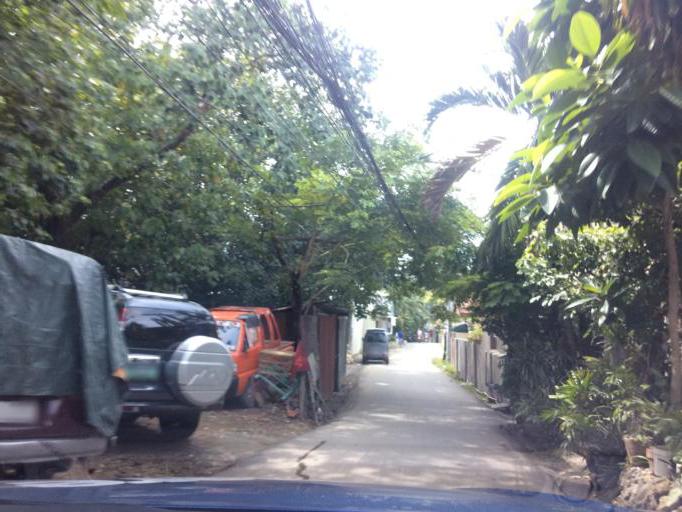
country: PH
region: Central Visayas
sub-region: Province of Cebu
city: Cebu City
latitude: 10.3214
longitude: 123.8963
